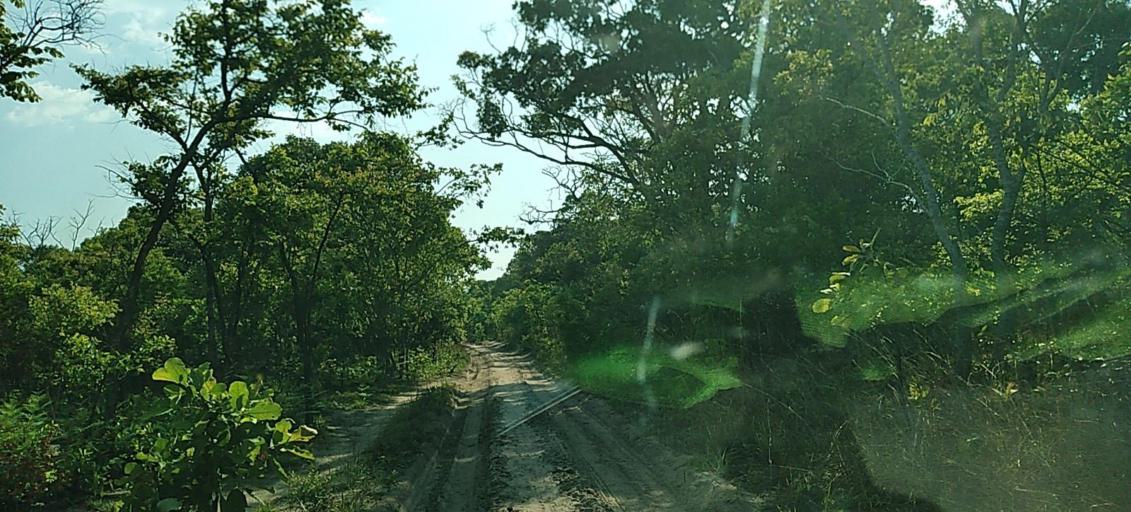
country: ZM
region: North-Western
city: Mwinilunga
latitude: -11.3152
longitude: 24.7432
